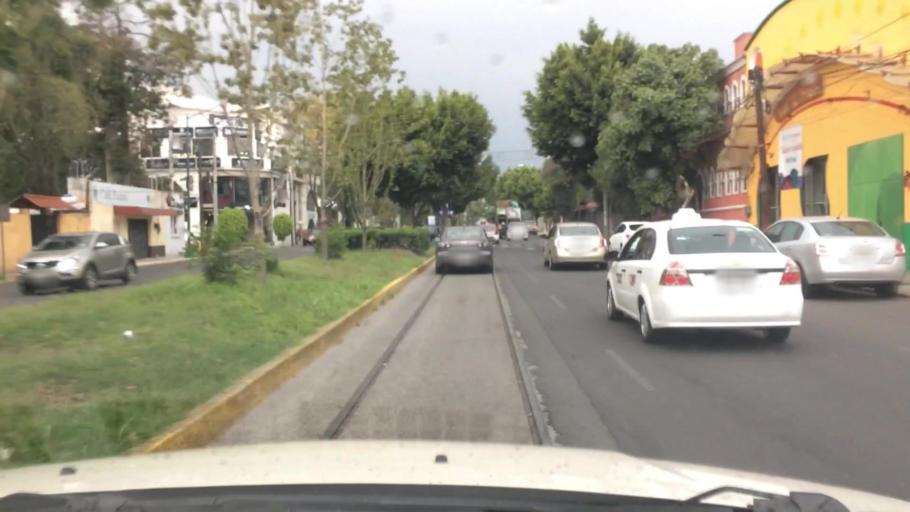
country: MX
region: Mexico City
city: Tlalpan
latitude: 19.2953
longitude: -99.1609
